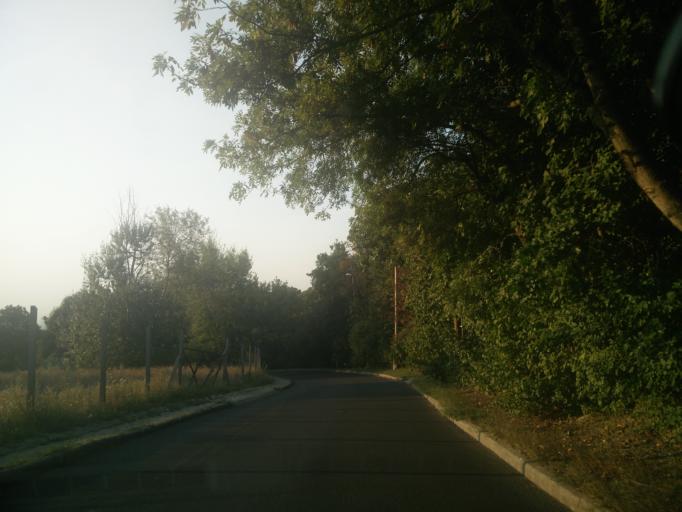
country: HU
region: Budapest
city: Budapest XII. keruelet
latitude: 47.4922
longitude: 18.9959
